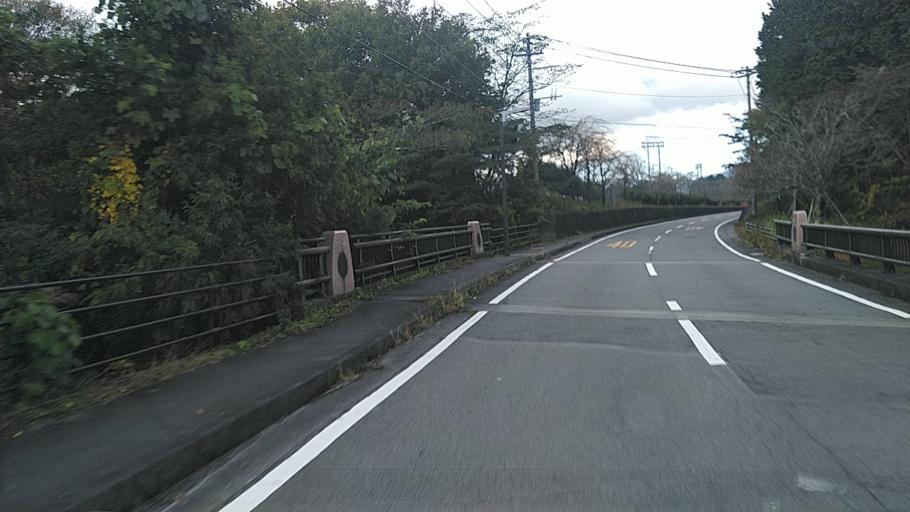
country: JP
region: Shizuoka
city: Gotemba
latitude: 35.3192
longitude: 138.9597
